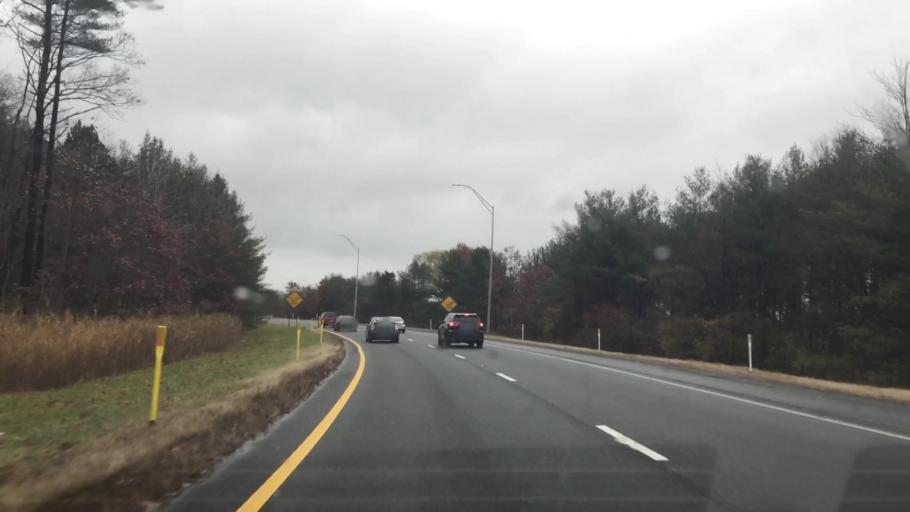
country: US
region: Massachusetts
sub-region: Essex County
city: Salisbury
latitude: 42.8596
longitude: -70.8925
